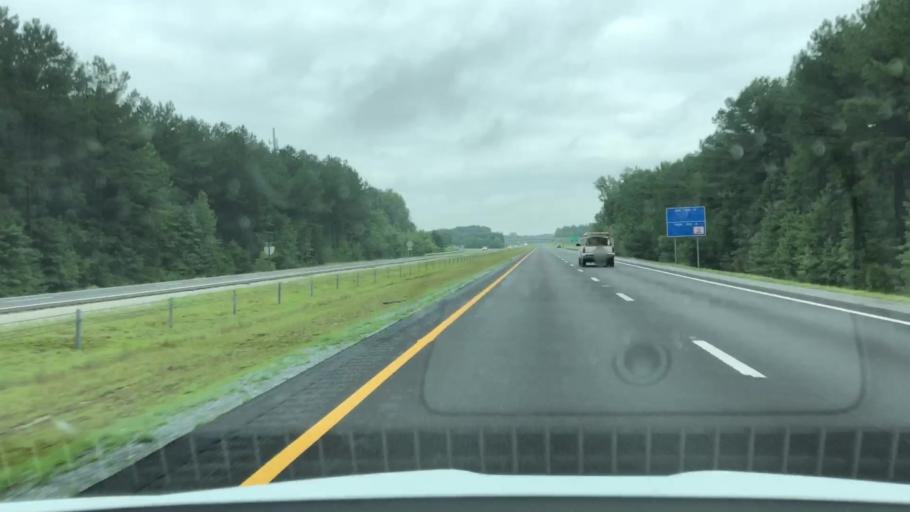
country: US
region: North Carolina
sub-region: Wayne County
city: Fremont
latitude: 35.4876
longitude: -77.9925
